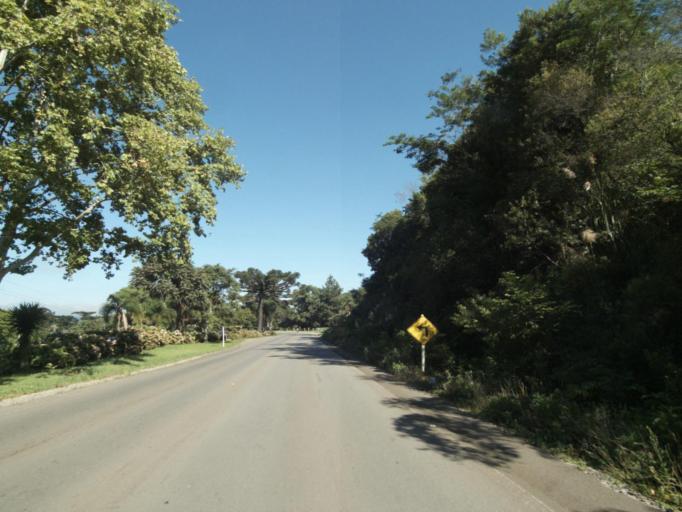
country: BR
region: Rio Grande do Sul
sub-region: Bento Goncalves
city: Bento Goncalves
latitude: -29.1150
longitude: -51.5801
